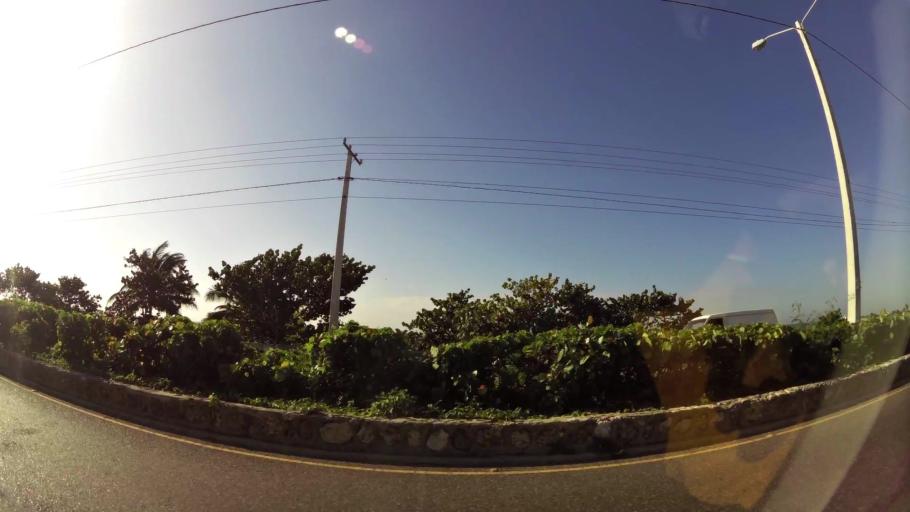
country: DO
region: Santo Domingo
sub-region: Santo Domingo
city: Santo Domingo Este
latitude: 18.4671
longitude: -69.8713
